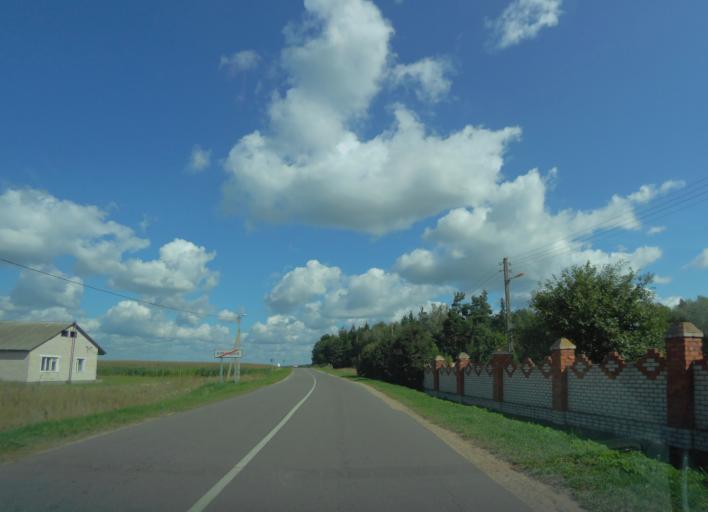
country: BY
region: Minsk
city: Zyembin
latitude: 54.3818
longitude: 28.3876
